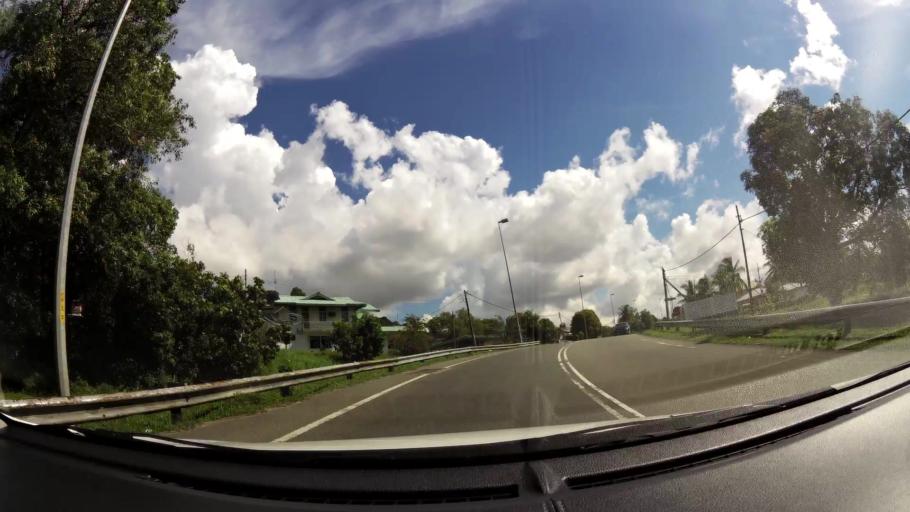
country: BN
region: Brunei and Muara
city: Bandar Seri Begawan
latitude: 4.9625
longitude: 114.9467
